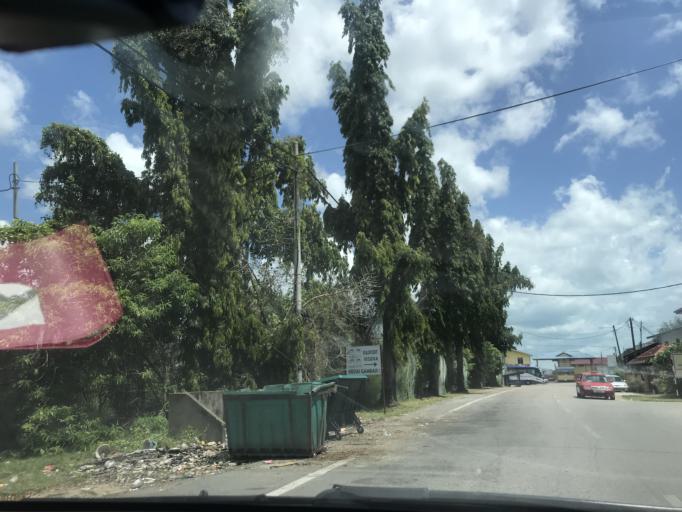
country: TH
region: Narathiwat
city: Tak Bai
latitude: 6.2322
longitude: 102.0929
